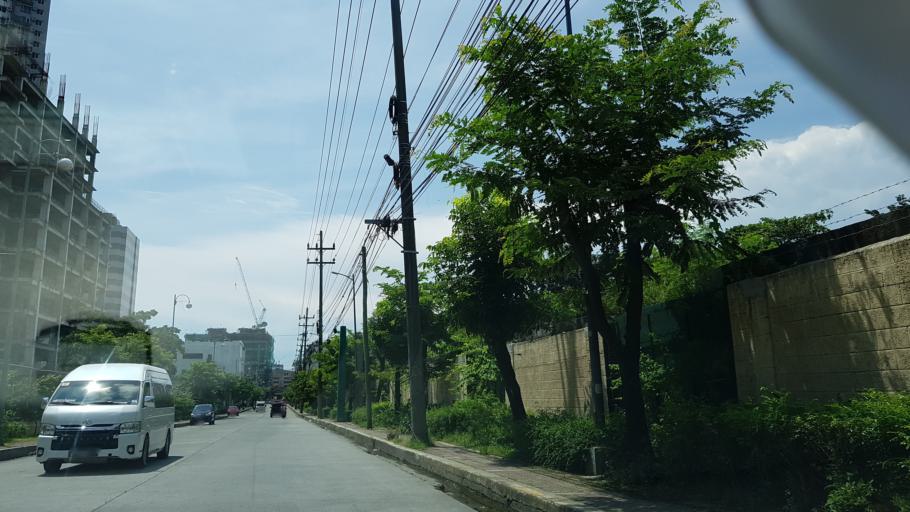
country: PH
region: Metro Manila
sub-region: Makati City
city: Makati City
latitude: 14.5633
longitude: 121.0190
